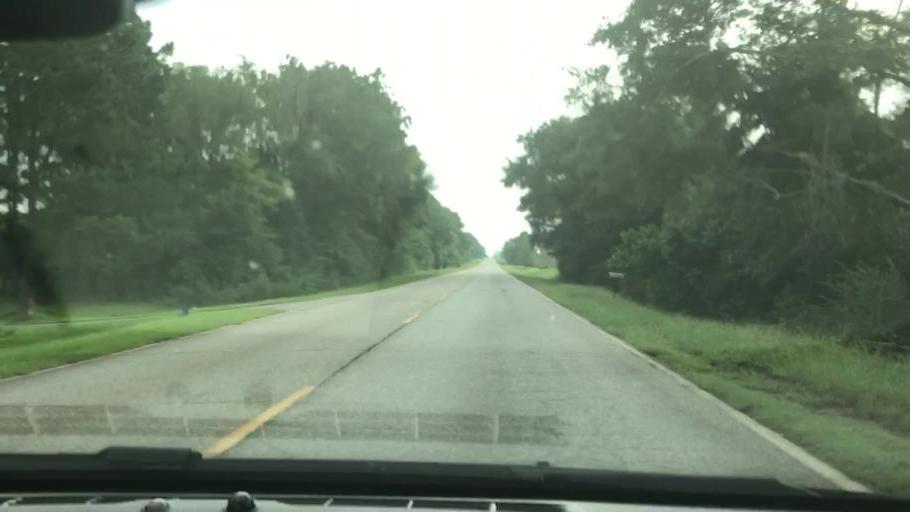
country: US
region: Georgia
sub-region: Quitman County
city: Georgetown
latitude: 31.8975
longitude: -85.0525
